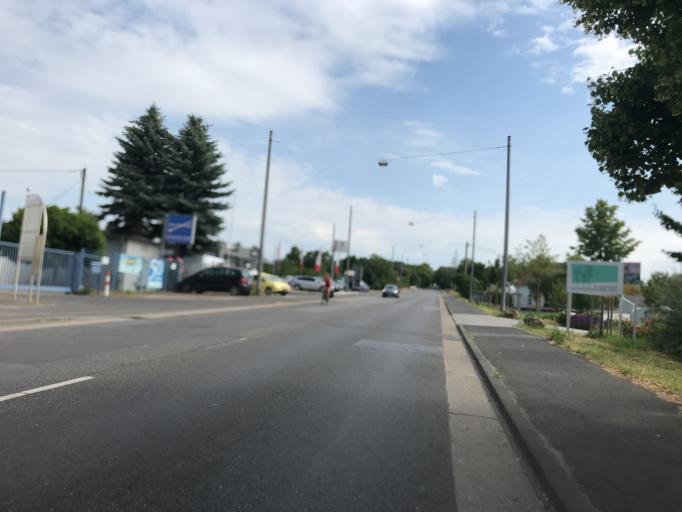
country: DE
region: Rheinland-Pfalz
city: Budenheim
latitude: 50.0508
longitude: 8.2049
